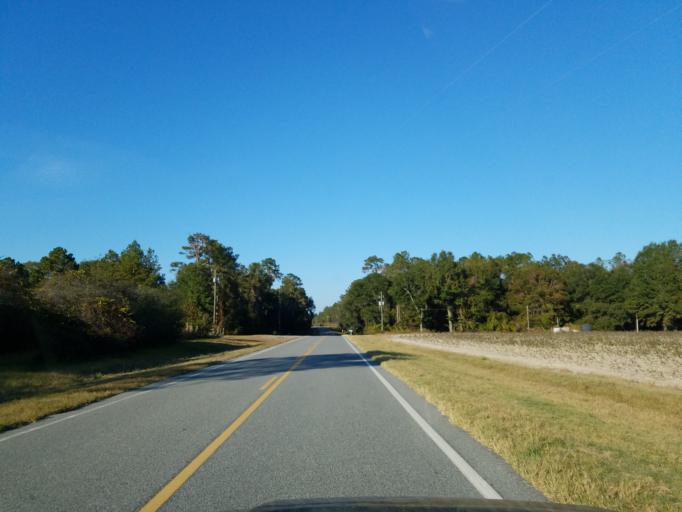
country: US
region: Georgia
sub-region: Echols County
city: Statenville
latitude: 30.6576
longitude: -83.0624
